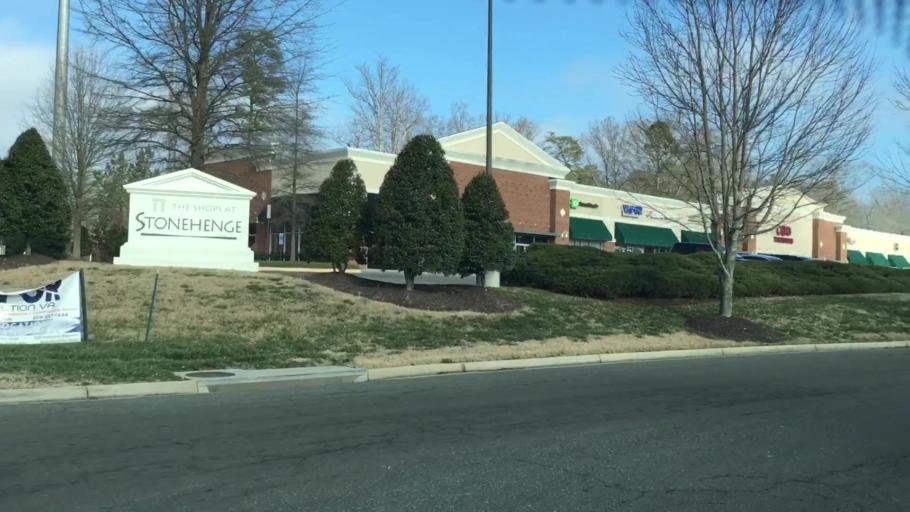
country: US
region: Virginia
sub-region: Chesterfield County
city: Bon Air
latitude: 37.5057
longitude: -77.6286
